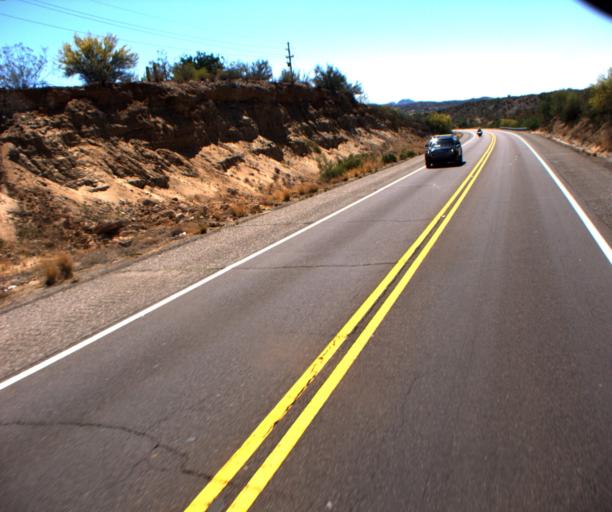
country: US
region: Arizona
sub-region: Maricopa County
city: Wickenburg
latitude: 33.9952
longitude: -112.7549
